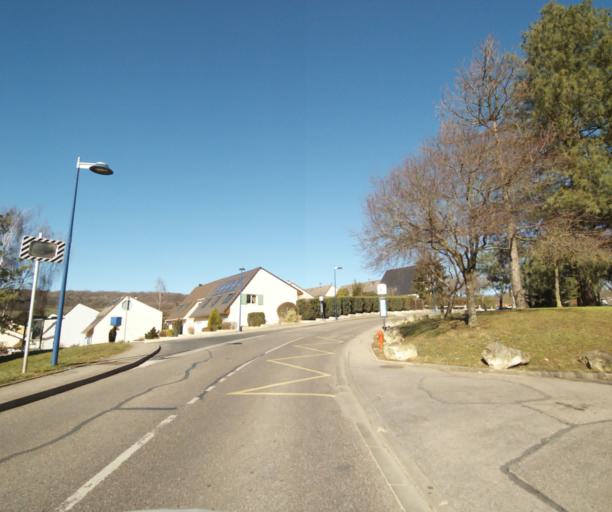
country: FR
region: Lorraine
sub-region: Departement de Meurthe-et-Moselle
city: Ludres
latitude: 48.6149
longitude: 6.1644
